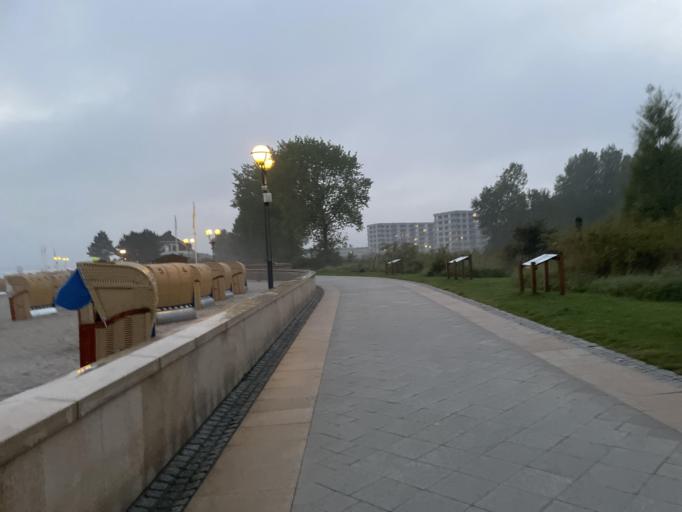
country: DE
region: Schleswig-Holstein
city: Gromitz
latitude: 54.1510
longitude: 10.9818
